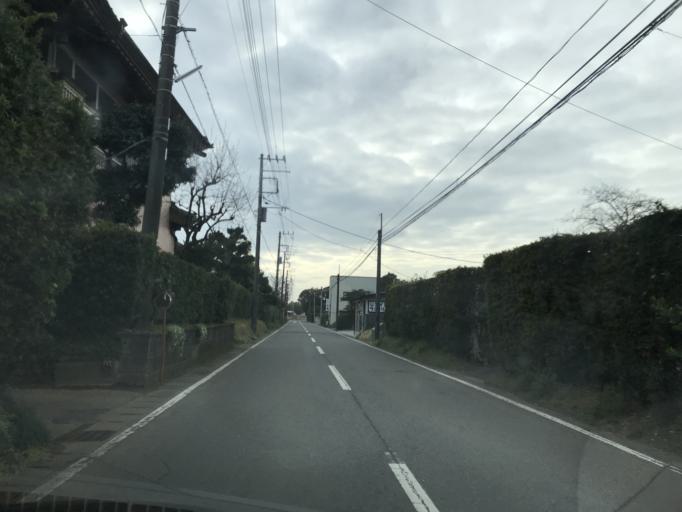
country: JP
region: Chiba
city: Omigawa
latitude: 35.7940
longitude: 140.5994
